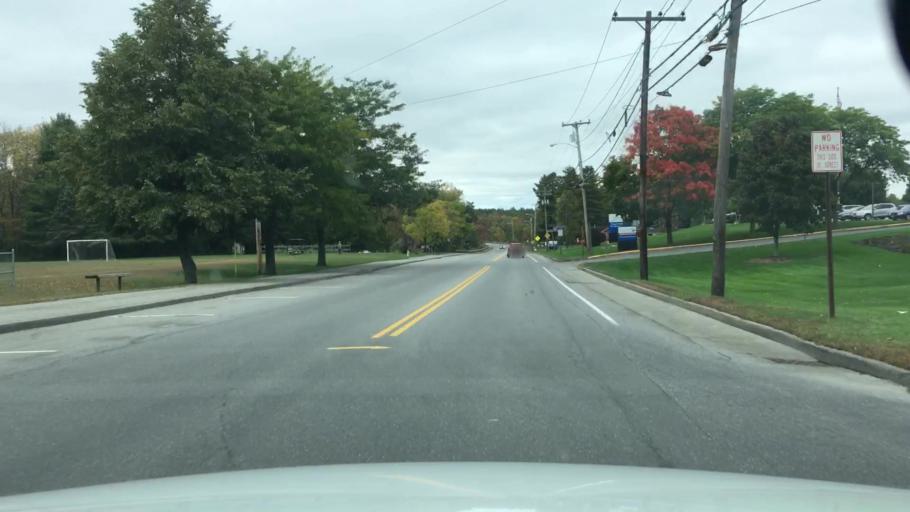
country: US
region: Maine
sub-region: Kennebec County
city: Waterville
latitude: 44.5639
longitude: -69.6468
